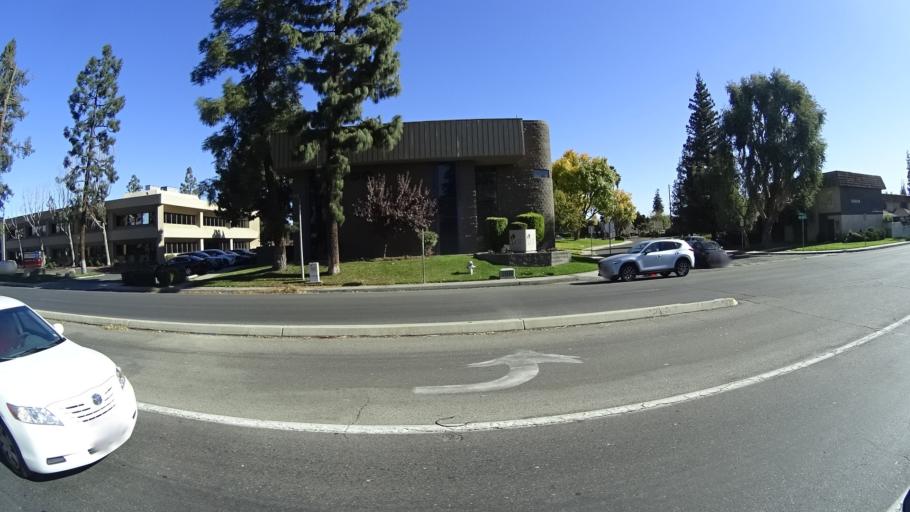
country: US
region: California
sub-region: Kern County
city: Bakersfield
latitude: 35.3520
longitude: -119.0613
